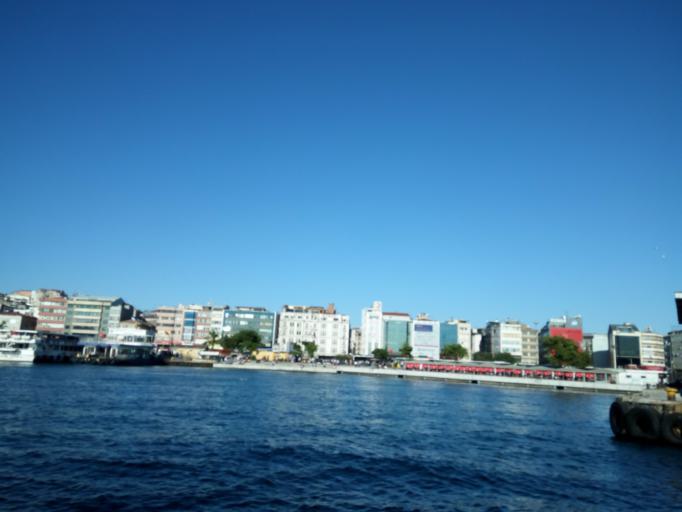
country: TR
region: Istanbul
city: UEskuedar
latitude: 40.9933
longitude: 29.0223
